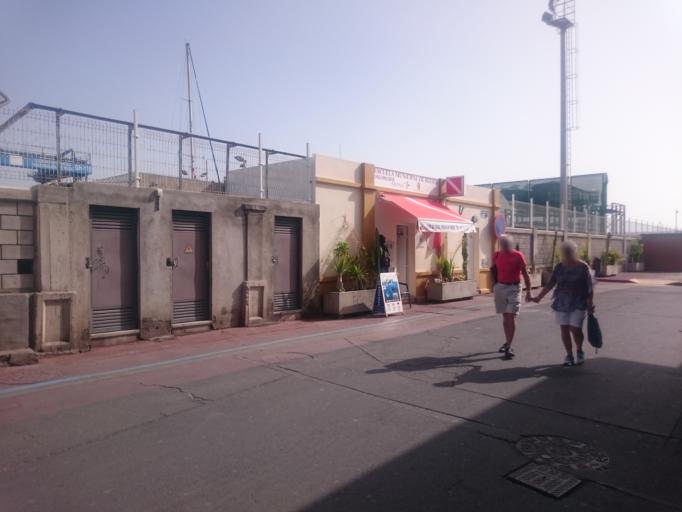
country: ES
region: Canary Islands
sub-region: Provincia de Santa Cruz de Tenerife
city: Playa de las Americas
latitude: 28.0500
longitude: -16.7198
